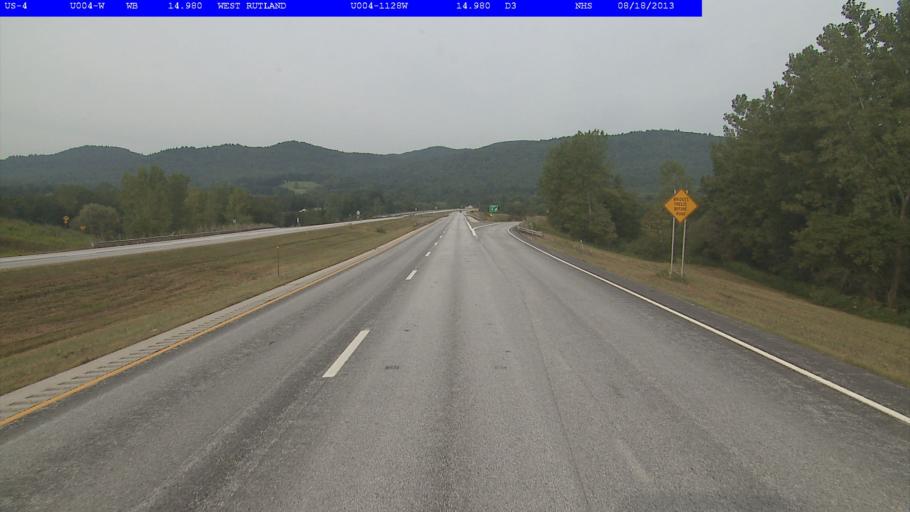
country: US
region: Vermont
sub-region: Rutland County
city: West Rutland
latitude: 43.5893
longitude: -73.0364
